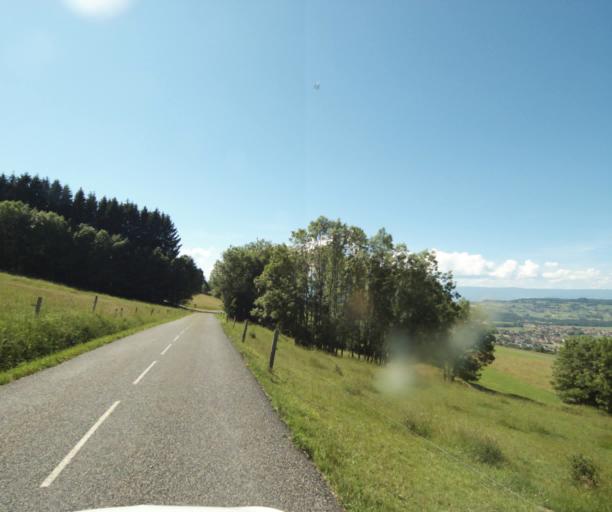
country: FR
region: Rhone-Alpes
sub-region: Departement de la Haute-Savoie
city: Bons-en-Chablais
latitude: 46.2498
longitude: 6.3715
